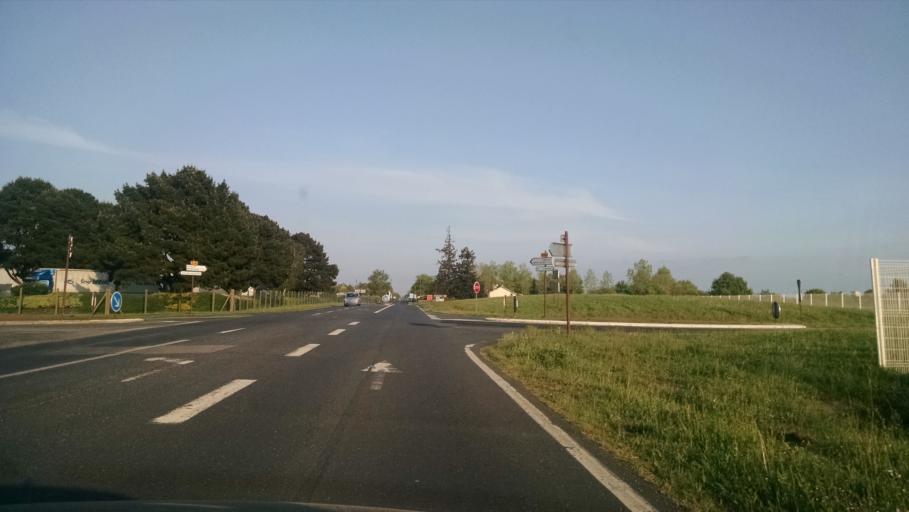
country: FR
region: Pays de la Loire
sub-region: Departement de la Loire-Atlantique
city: Boussay
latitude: 47.0604
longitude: -1.1865
